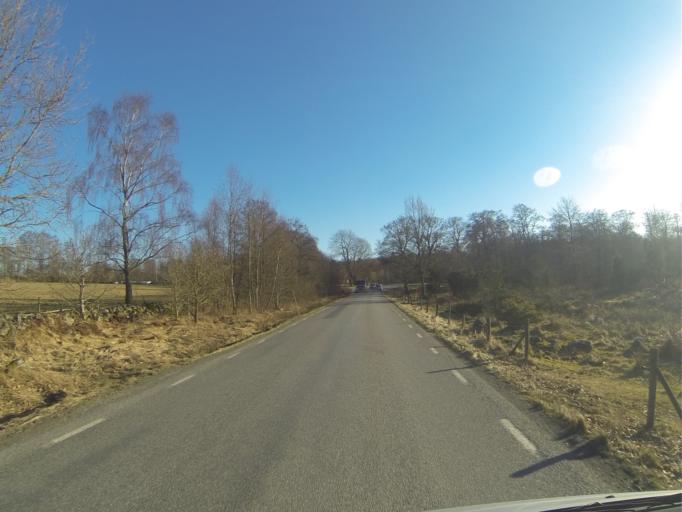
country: SE
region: Skane
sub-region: Horby Kommun
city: Hoerby
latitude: 55.8912
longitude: 13.6669
